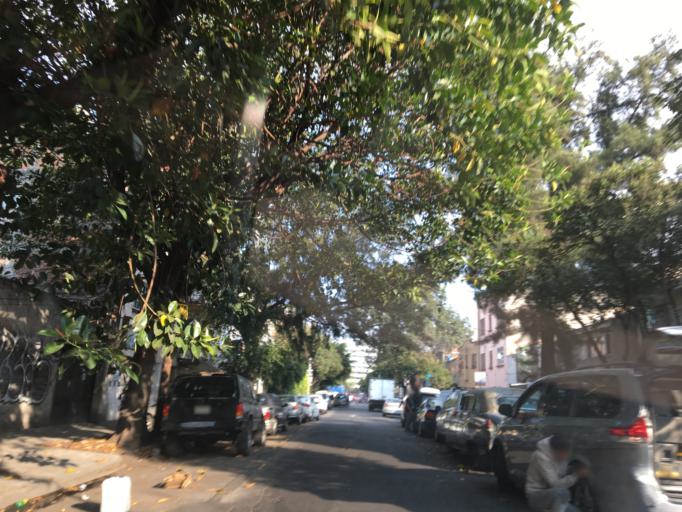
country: MX
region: Mexico City
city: Mexico City
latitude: 19.4173
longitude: -99.1374
